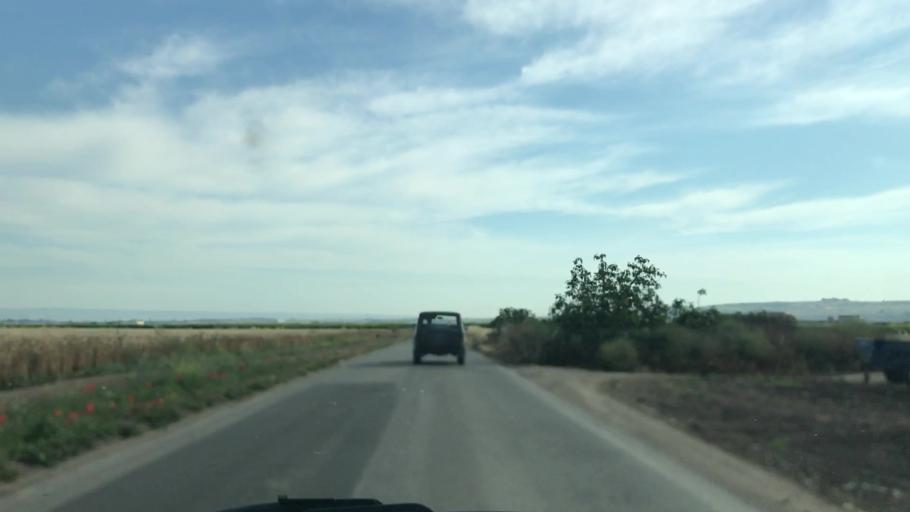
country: IT
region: Apulia
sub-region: Provincia di Taranto
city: San Giorgio Ionico
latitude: 40.4330
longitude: 17.3451
